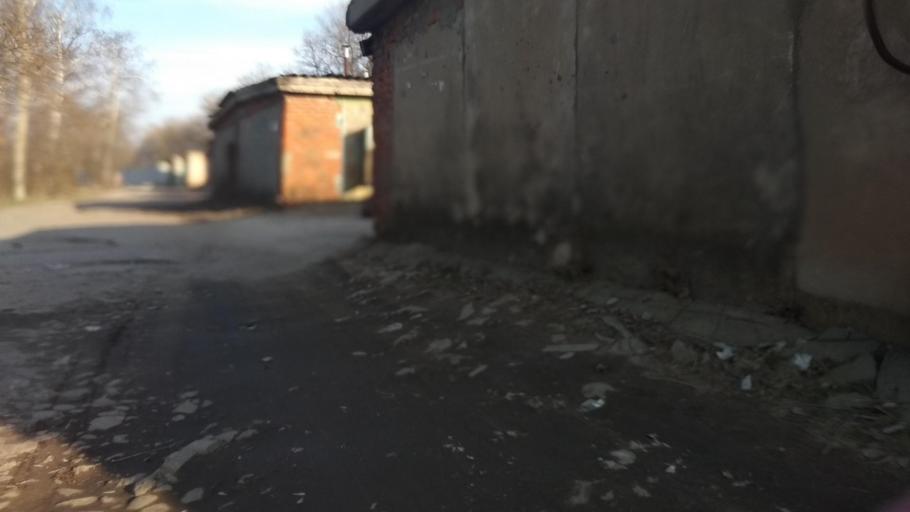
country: RU
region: Moskovskaya
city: Razvilka
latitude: 55.5813
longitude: 37.7261
